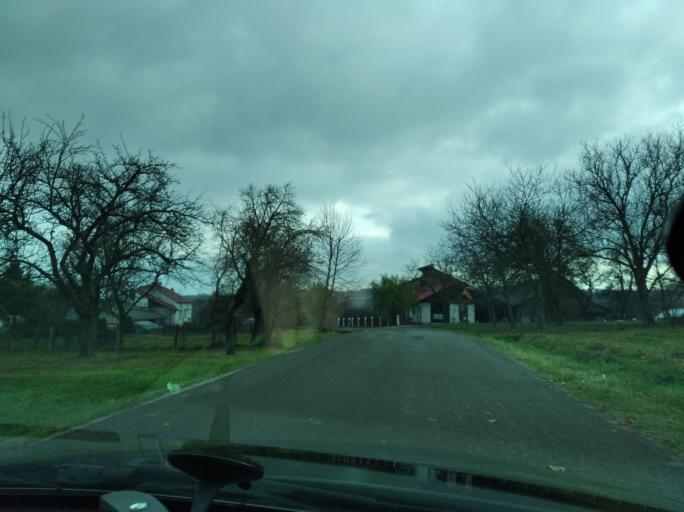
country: PL
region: Subcarpathian Voivodeship
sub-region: Powiat przeworski
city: Sietesz
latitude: 49.9714
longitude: 22.3376
